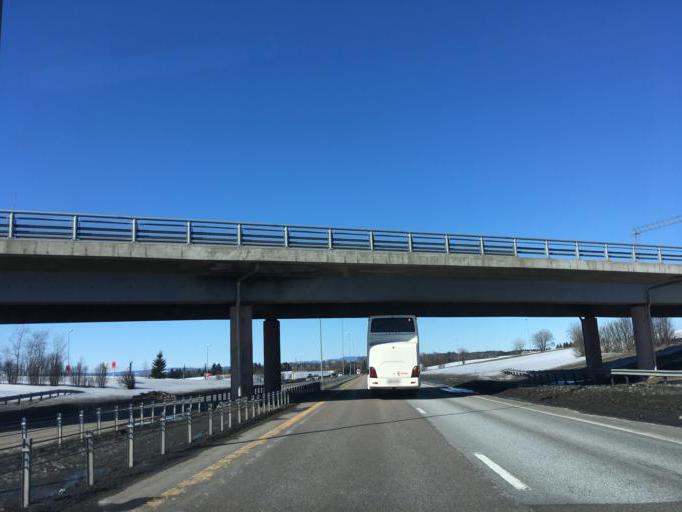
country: NO
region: Akershus
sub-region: Ullensaker
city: Jessheim
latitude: 60.1311
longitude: 11.1620
